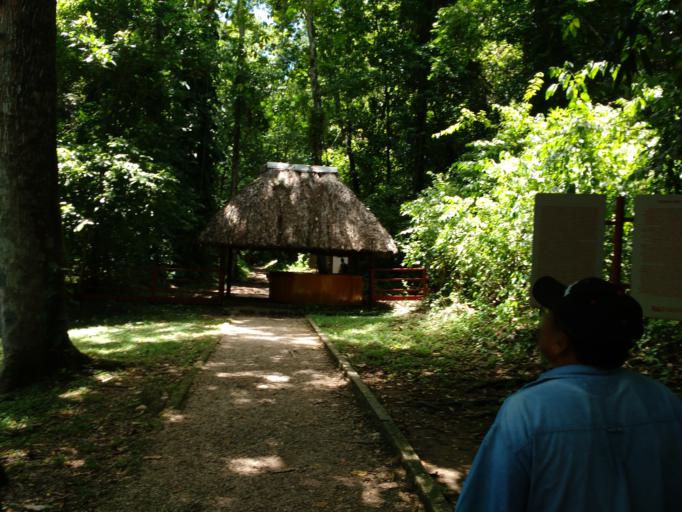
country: MX
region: Chiapas
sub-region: Ocosingo
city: Frontera Corozal
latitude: 16.9013
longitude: -90.9677
